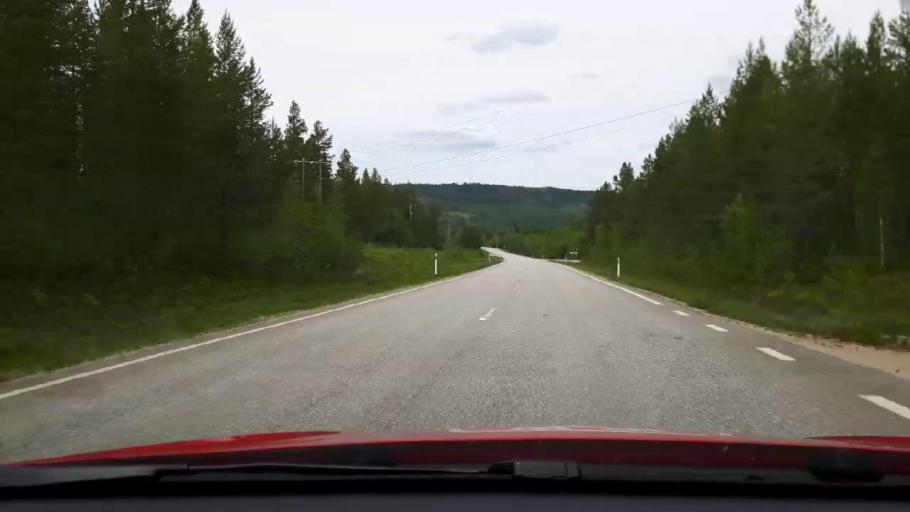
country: SE
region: Jaemtland
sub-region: Harjedalens Kommun
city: Sveg
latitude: 62.0875
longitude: 14.2497
